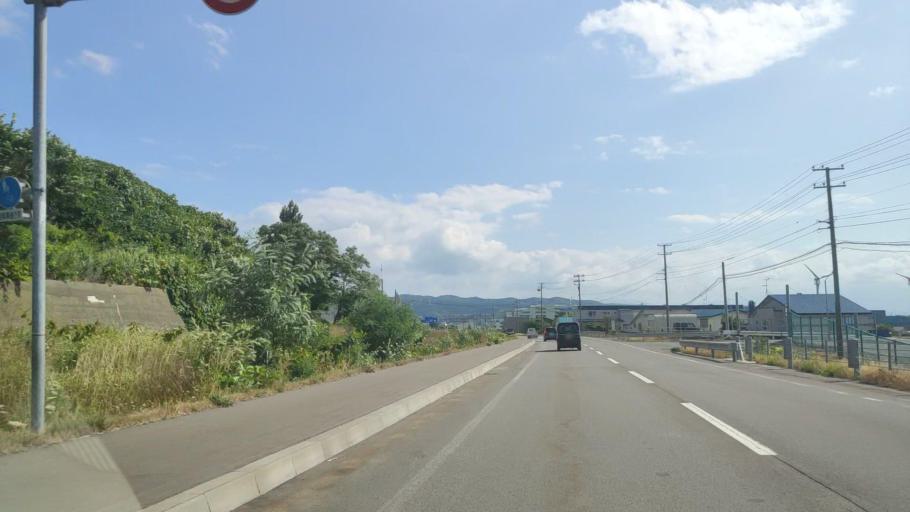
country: JP
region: Hokkaido
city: Rumoi
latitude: 43.9563
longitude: 141.6440
